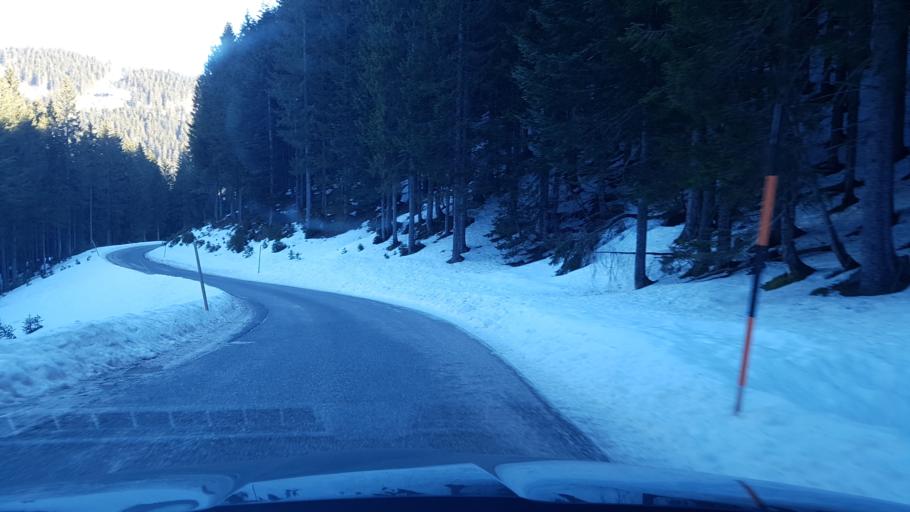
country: AT
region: Salzburg
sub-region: Politischer Bezirk Hallein
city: Abtenau
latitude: 47.6308
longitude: 13.4139
